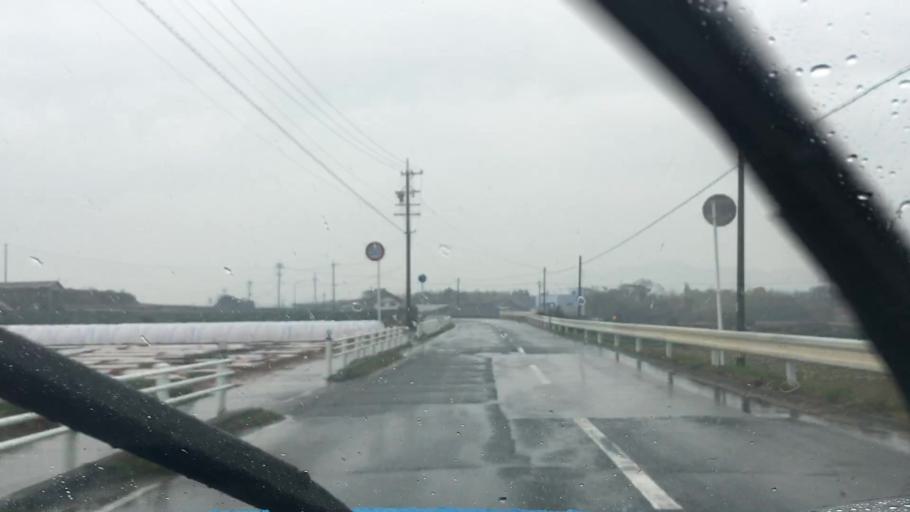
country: JP
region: Aichi
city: Tahara
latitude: 34.6486
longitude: 137.3034
